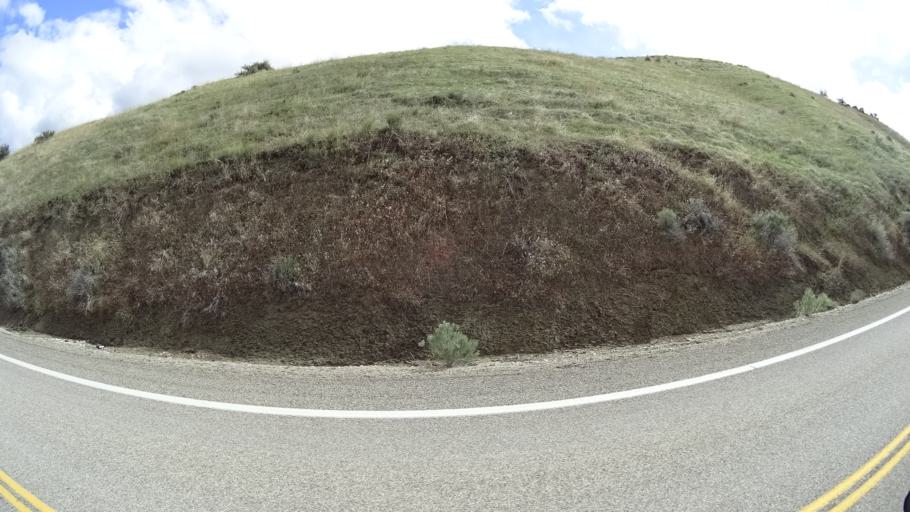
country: US
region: Idaho
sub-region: Ada County
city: Garden City
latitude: 43.7021
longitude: -116.2322
